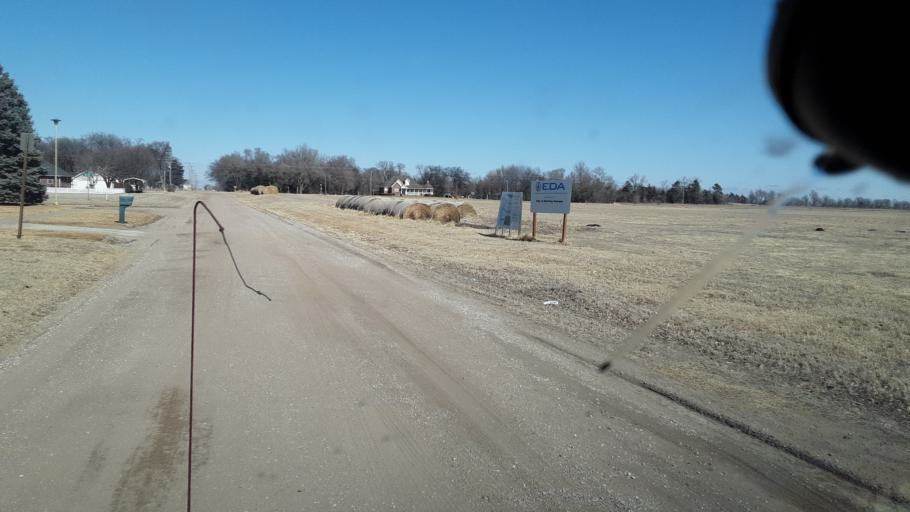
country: US
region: Kansas
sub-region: Rice County
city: Sterling
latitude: 38.2149
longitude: -98.1976
